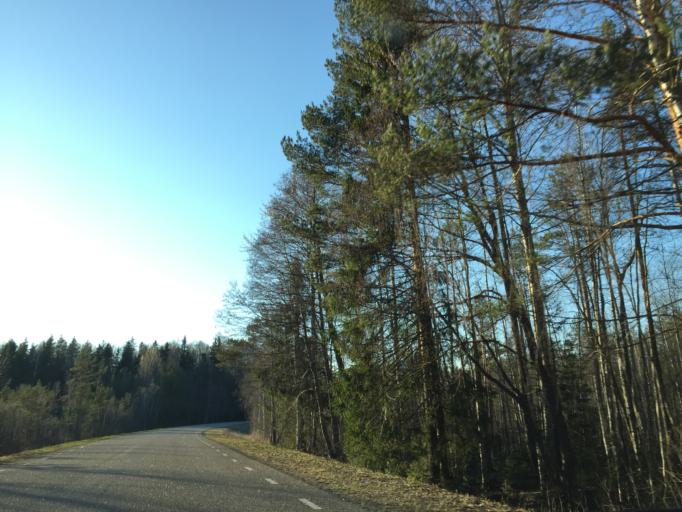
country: EE
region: Ida-Virumaa
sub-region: Toila vald
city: Voka
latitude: 59.1278
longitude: 27.6151
